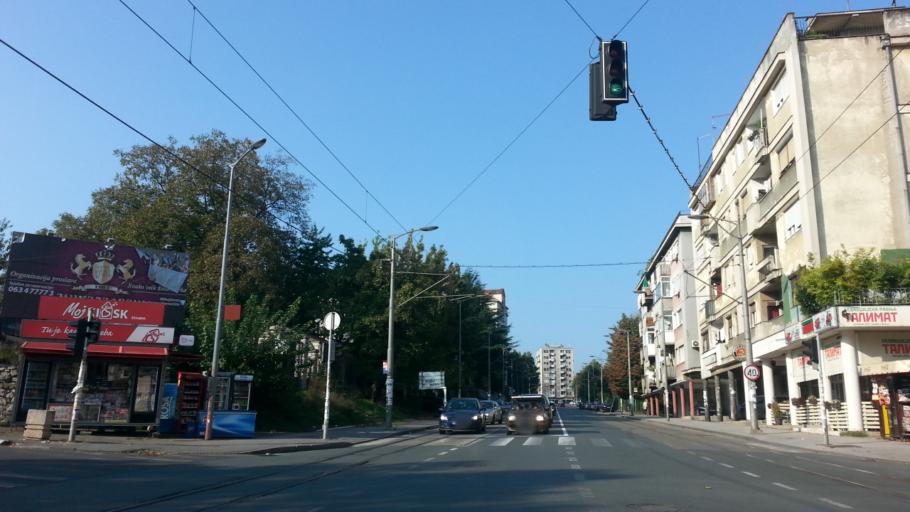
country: RS
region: Central Serbia
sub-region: Belgrade
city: Cukarica
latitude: 44.7831
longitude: 20.4227
